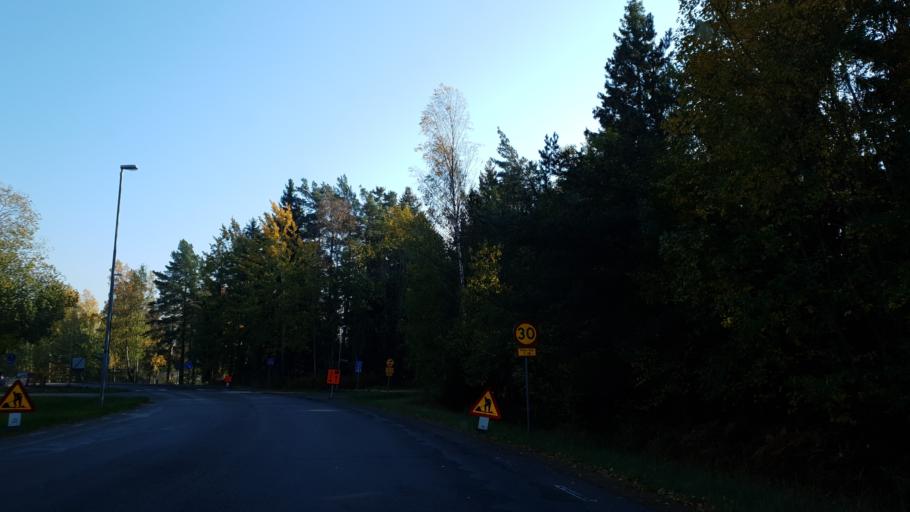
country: SE
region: Stockholm
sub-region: Haninge Kommun
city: Haninge
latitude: 59.1719
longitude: 18.1882
